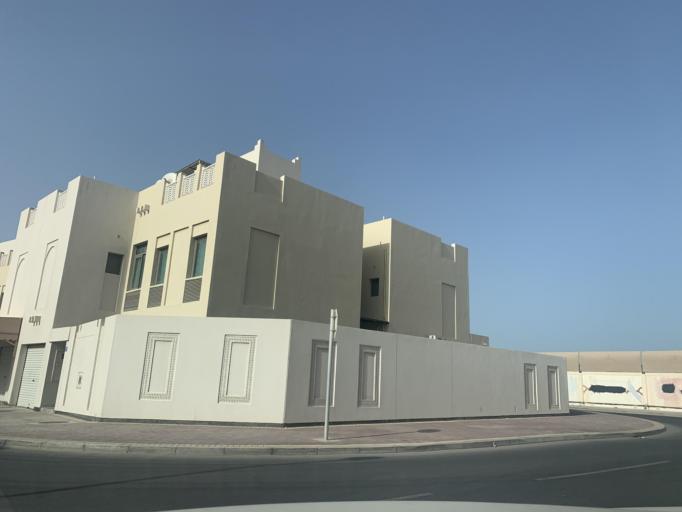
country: BH
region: Northern
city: Sitrah
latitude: 26.1627
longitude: 50.6285
